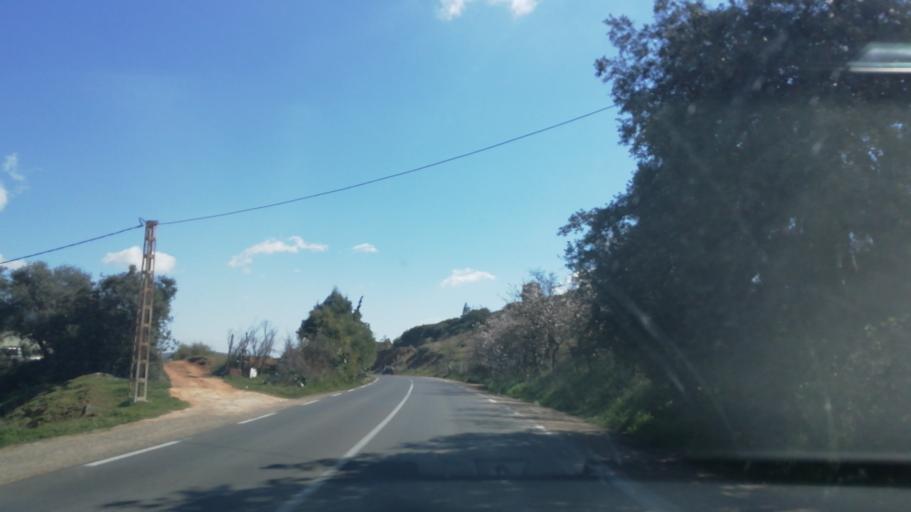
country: DZ
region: Mascara
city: Mascara
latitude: 35.4576
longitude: 0.1498
